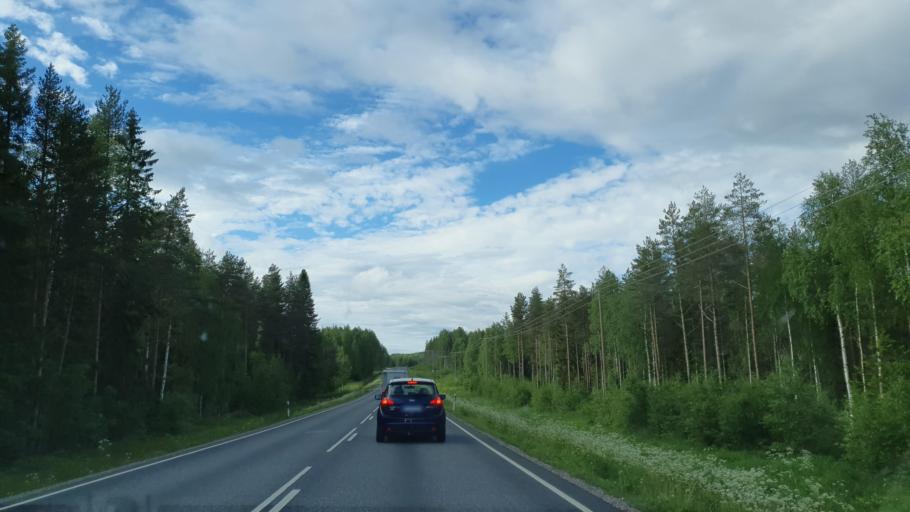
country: FI
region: Kainuu
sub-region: Kajaani
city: Paltamo
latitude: 64.4438
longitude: 27.8145
